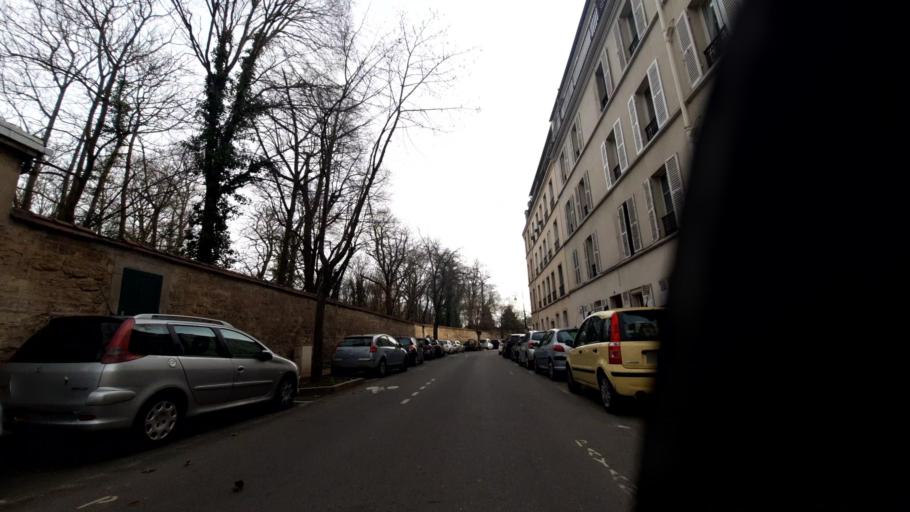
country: FR
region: Ile-de-France
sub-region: Departement du Val-de-Marne
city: Saint-Maurice
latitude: 48.8215
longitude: 2.4234
